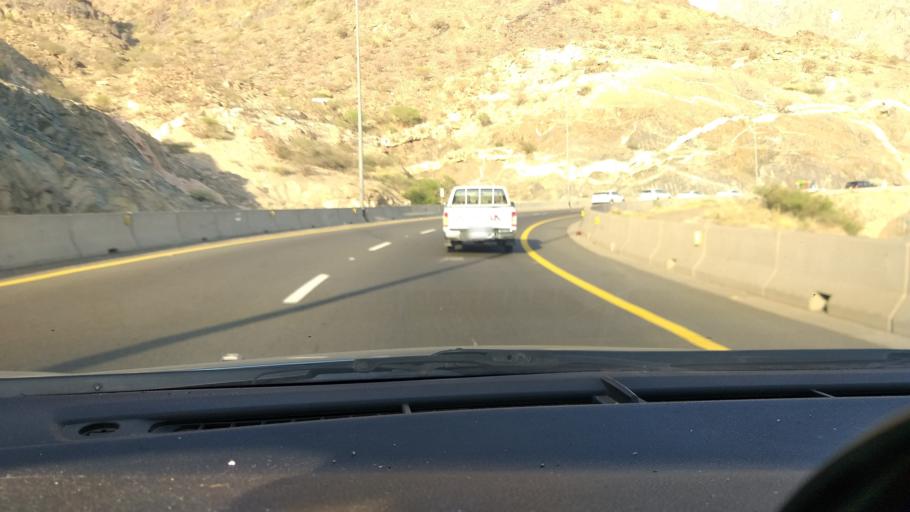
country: SA
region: Makkah
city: Al Hada
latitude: 21.3600
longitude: 40.2337
